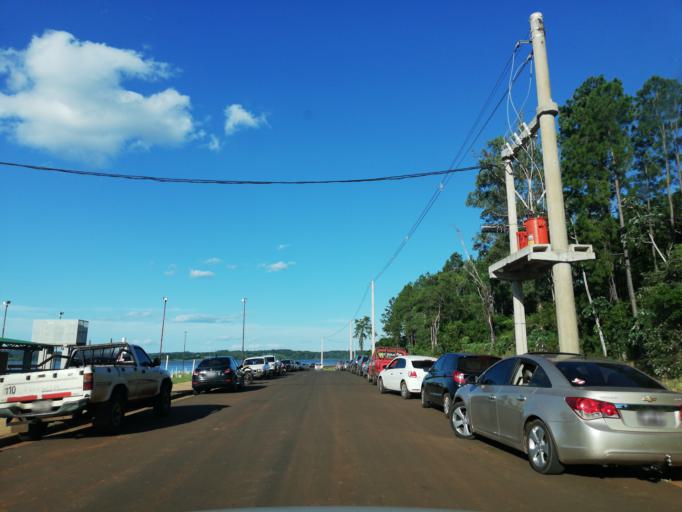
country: AR
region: Misiones
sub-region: Departamento de Candelaria
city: Candelaria
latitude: -27.4521
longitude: -55.7816
